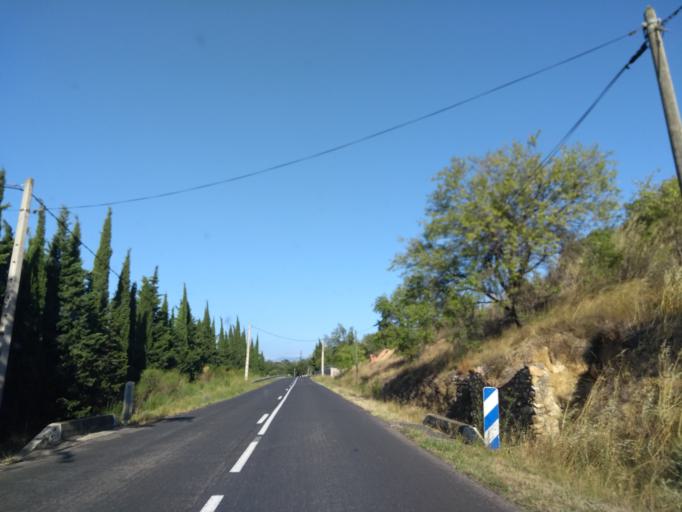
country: FR
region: Languedoc-Roussillon
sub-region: Departement des Pyrenees-Orientales
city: Millas
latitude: 42.7012
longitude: 2.7098
